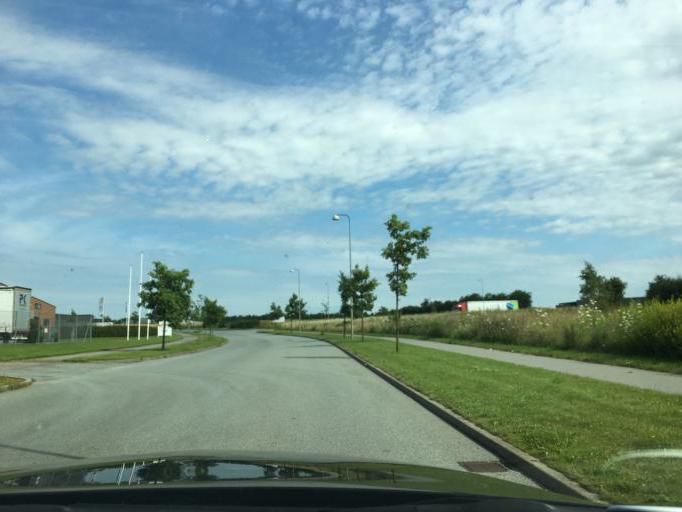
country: DK
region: South Denmark
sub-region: Kolding Kommune
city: Kolding
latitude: 55.5424
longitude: 9.4709
